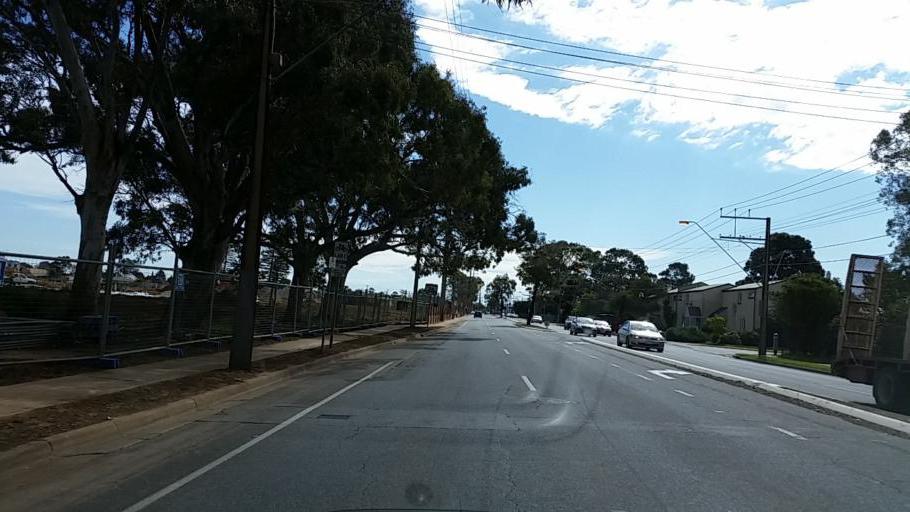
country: AU
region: South Australia
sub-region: Charles Sturt
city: Woodville North
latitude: -34.8665
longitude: 138.5340
